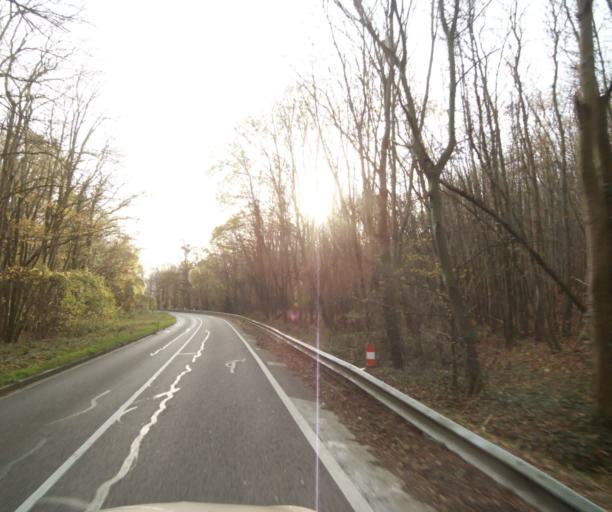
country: FR
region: Ile-de-France
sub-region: Departement des Yvelines
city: Triel-sur-Seine
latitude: 48.9958
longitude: 2.0063
